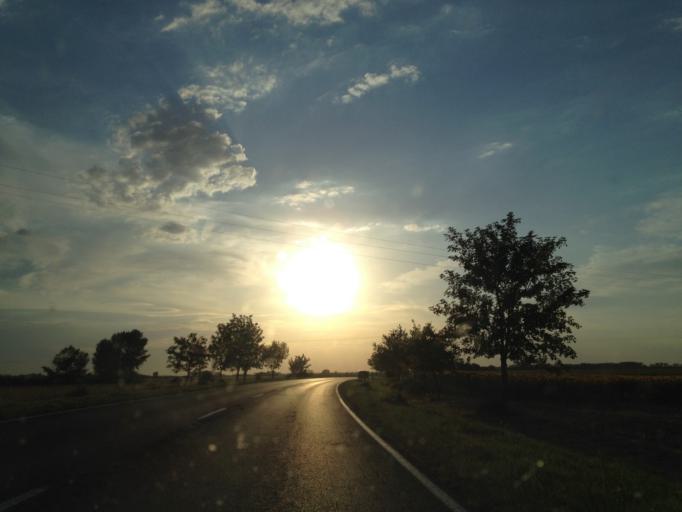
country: HU
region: Gyor-Moson-Sopron
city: Kimle
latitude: 47.8006
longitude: 17.3796
